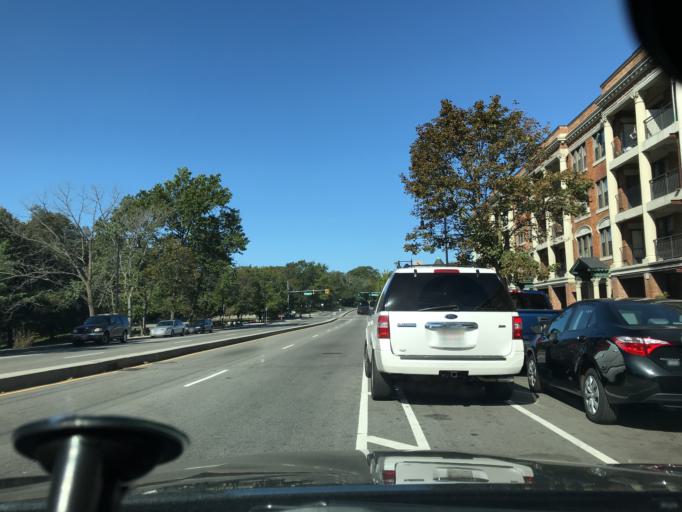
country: US
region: Massachusetts
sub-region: Suffolk County
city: Jamaica Plain
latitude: 42.3091
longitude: -71.0909
